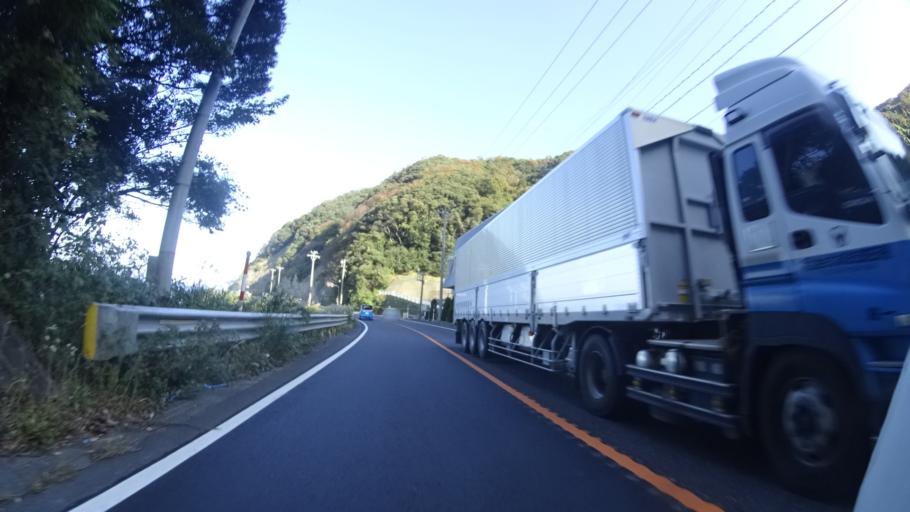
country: JP
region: Fukui
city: Tsuruga
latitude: 35.6928
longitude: 136.0817
